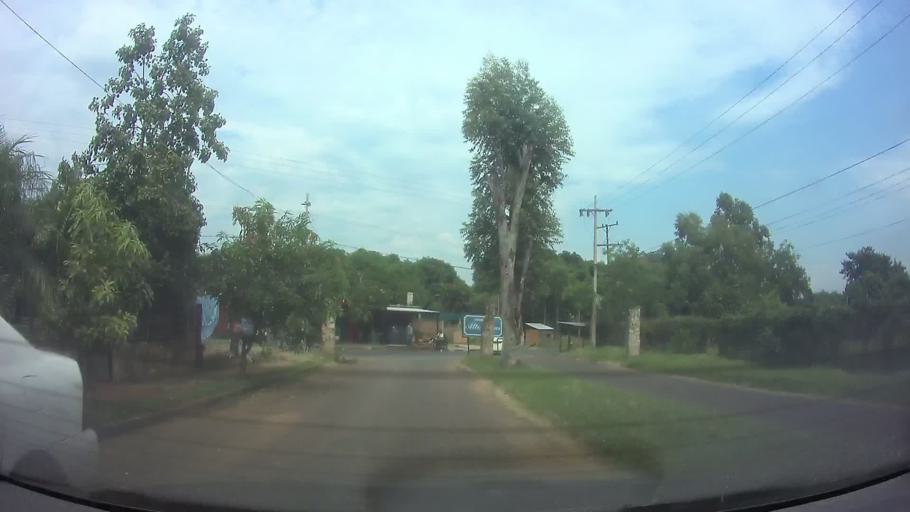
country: PY
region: Central
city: Fernando de la Mora
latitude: -25.2909
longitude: -57.5128
